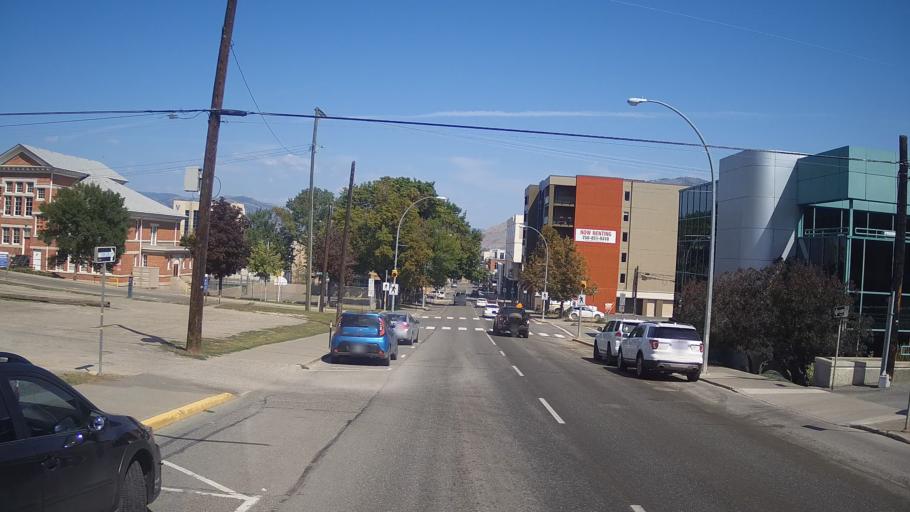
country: CA
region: British Columbia
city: Kamloops
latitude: 50.6726
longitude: -120.3345
